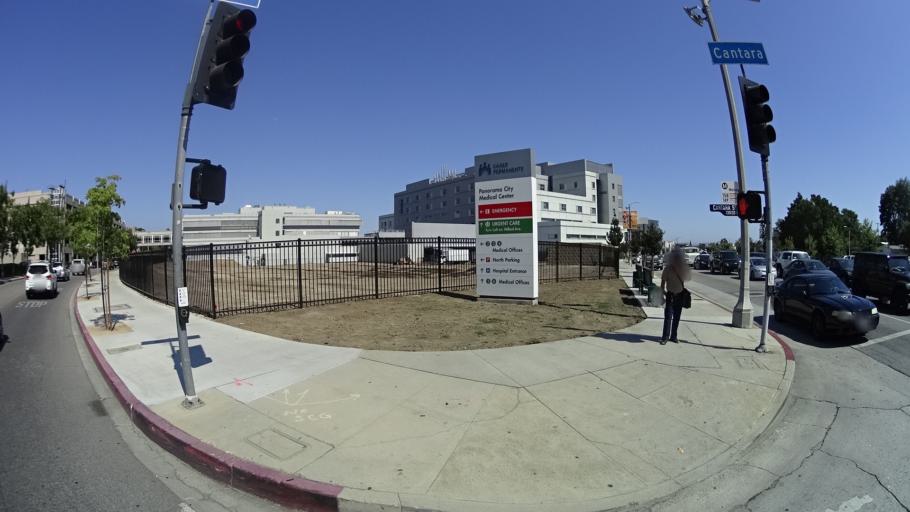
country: US
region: California
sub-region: Los Angeles County
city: Van Nuys
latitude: 34.2197
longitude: -118.4318
